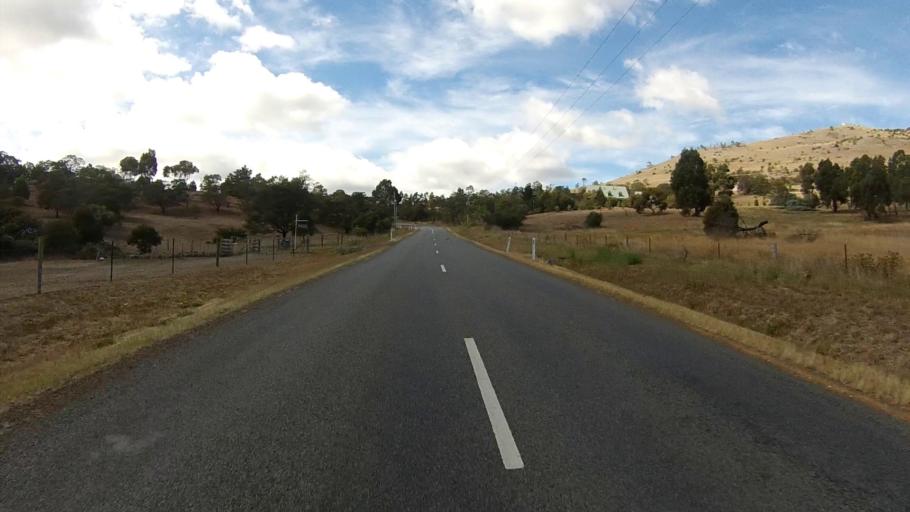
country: AU
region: Tasmania
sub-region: Glenorchy
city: Austins Ferry
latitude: -42.7251
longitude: 147.2840
